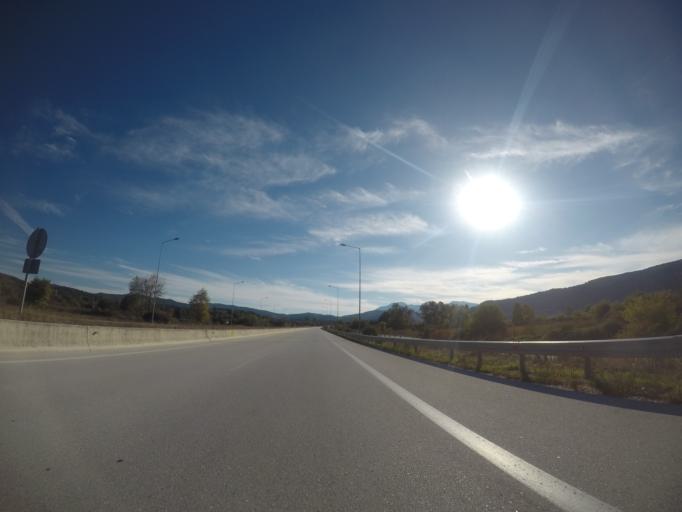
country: GR
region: Epirus
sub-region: Nomos Ioanninon
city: Koutselio
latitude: 39.6150
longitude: 20.9436
